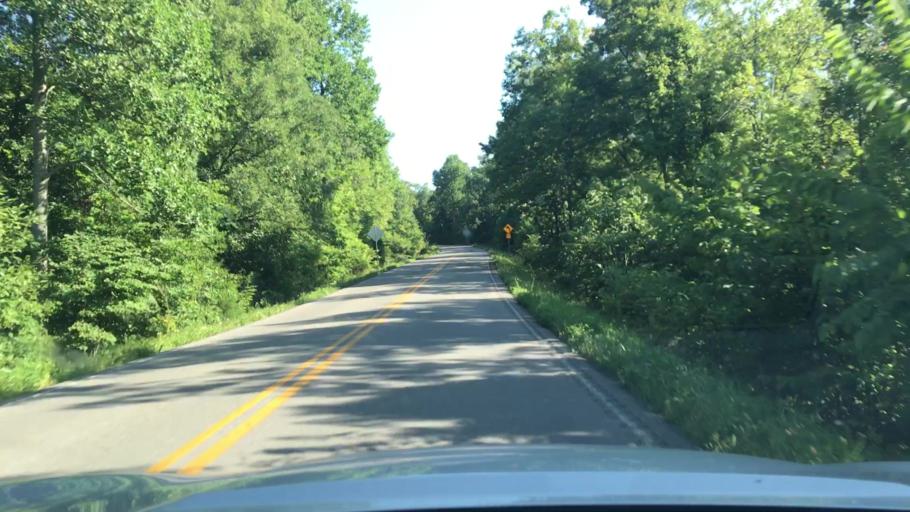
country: US
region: Kentucky
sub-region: Muhlenberg County
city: Greenville
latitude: 37.1099
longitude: -87.1277
